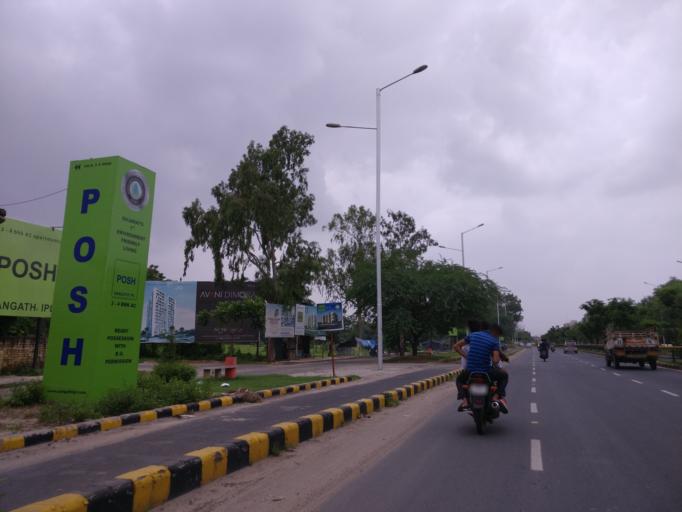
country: IN
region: Gujarat
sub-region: Gandhinagar
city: Adalaj
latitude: 23.1278
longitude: 72.5841
